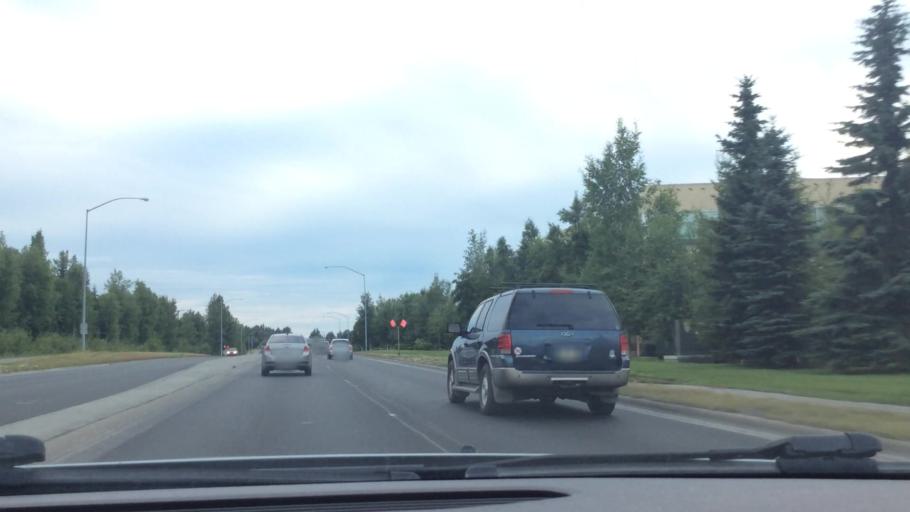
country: US
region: Alaska
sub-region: Anchorage Municipality
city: Anchorage
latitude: 61.1811
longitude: -149.7981
